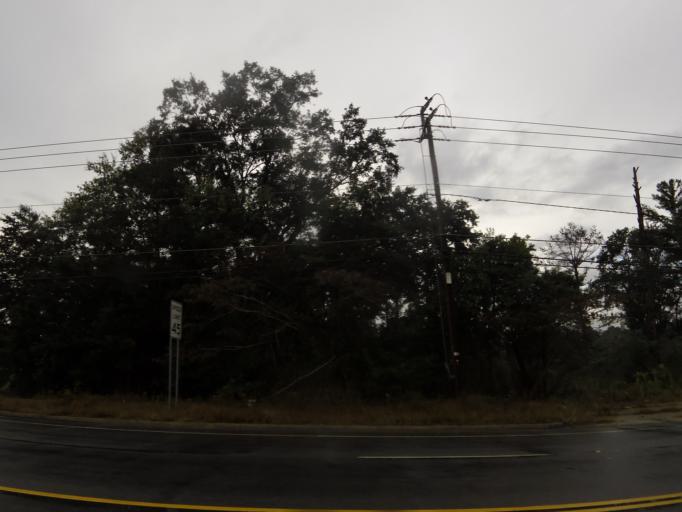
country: US
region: Georgia
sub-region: Wayne County
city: Jesup
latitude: 31.5896
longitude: -81.8735
